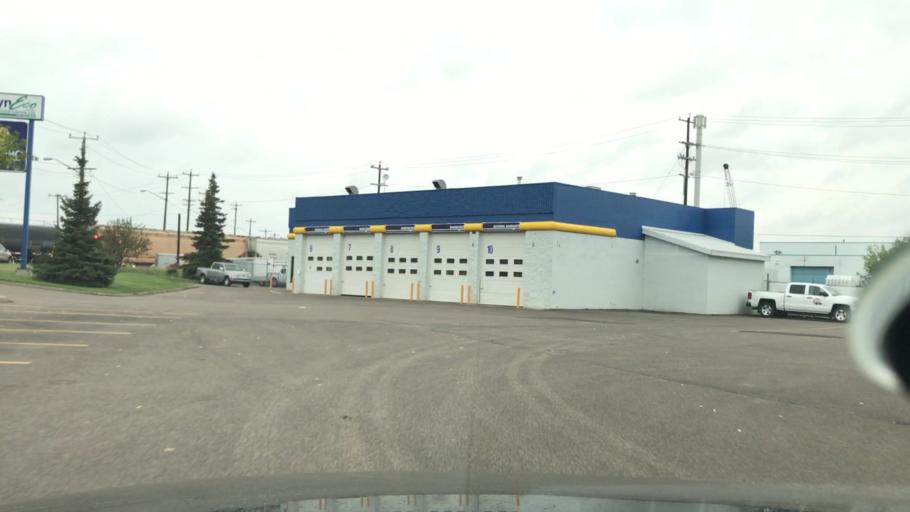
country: CA
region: Alberta
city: Edmonton
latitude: 53.5067
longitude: -113.4431
